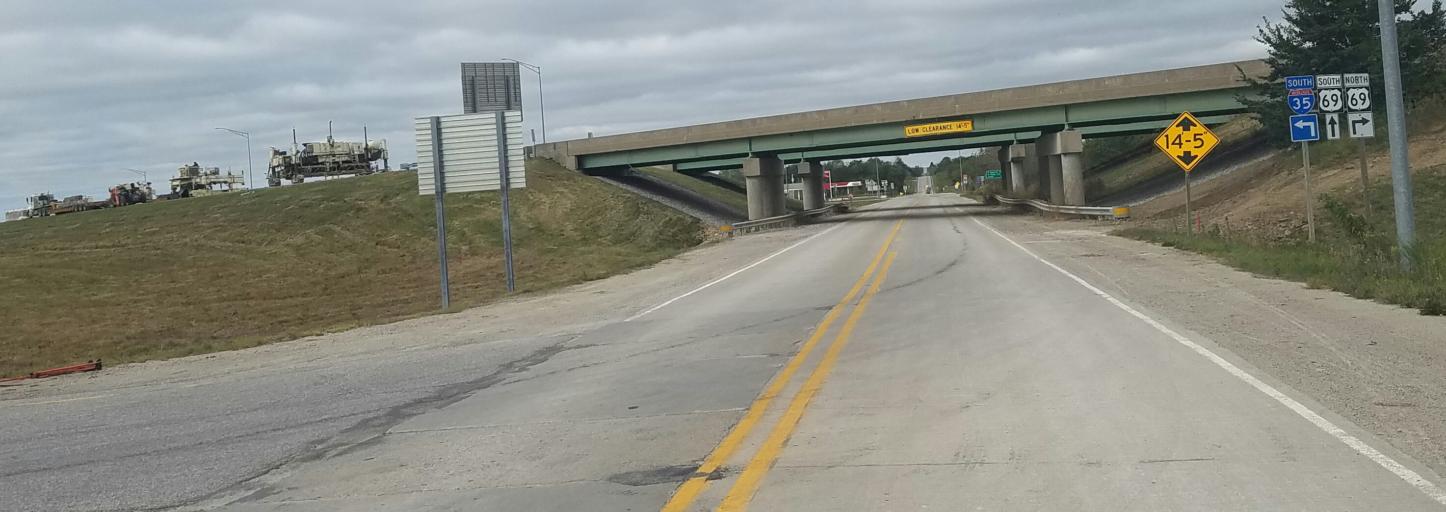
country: US
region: Iowa
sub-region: Decatur County
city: Lamoni
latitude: 40.5752
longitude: -93.9361
